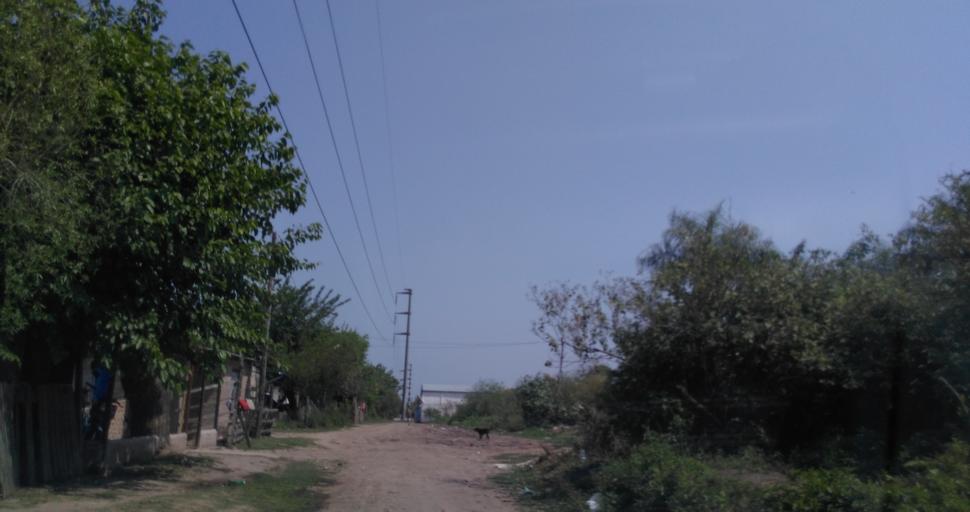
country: AR
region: Chaco
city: Fontana
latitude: -27.4162
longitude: -59.0211
